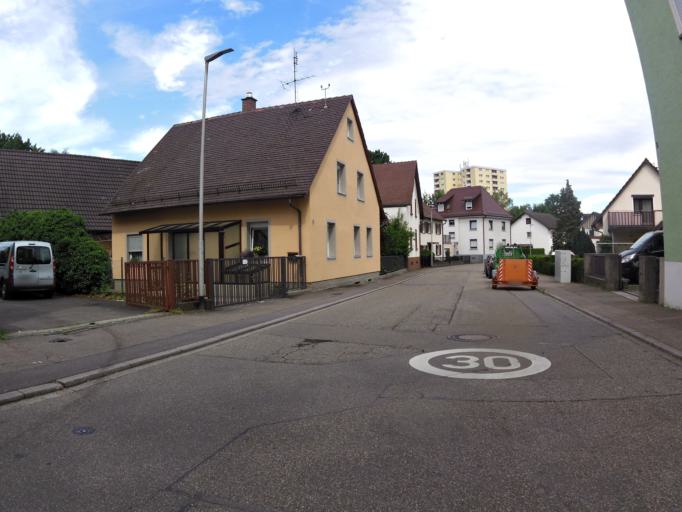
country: DE
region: Baden-Wuerttemberg
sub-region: Freiburg Region
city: Lahr
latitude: 48.3436
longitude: 7.8413
